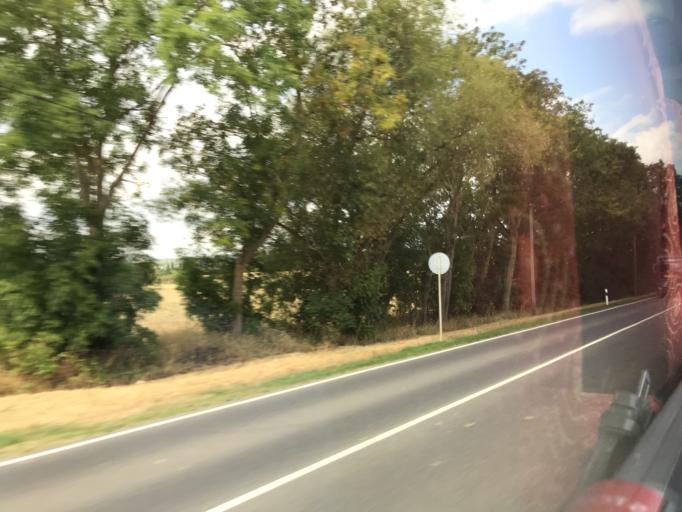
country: LU
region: Luxembourg
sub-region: Canton de Luxembourg
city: Alzingen
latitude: 49.5522
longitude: 6.1720
